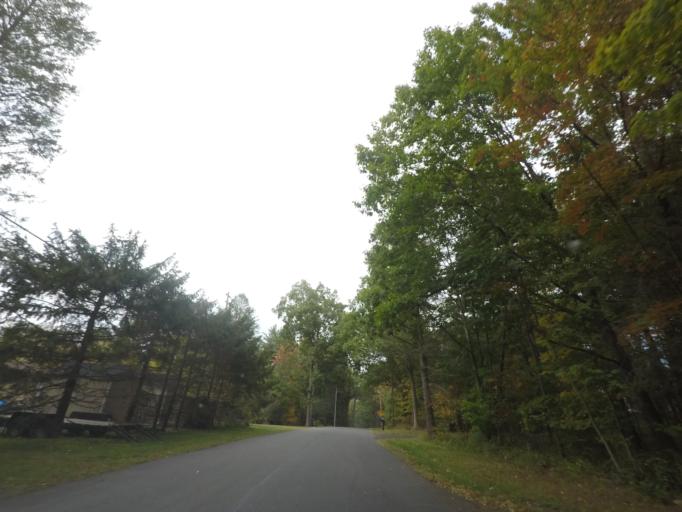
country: US
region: New York
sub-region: Rensselaer County
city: Nassau
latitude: 42.5413
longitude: -73.6472
